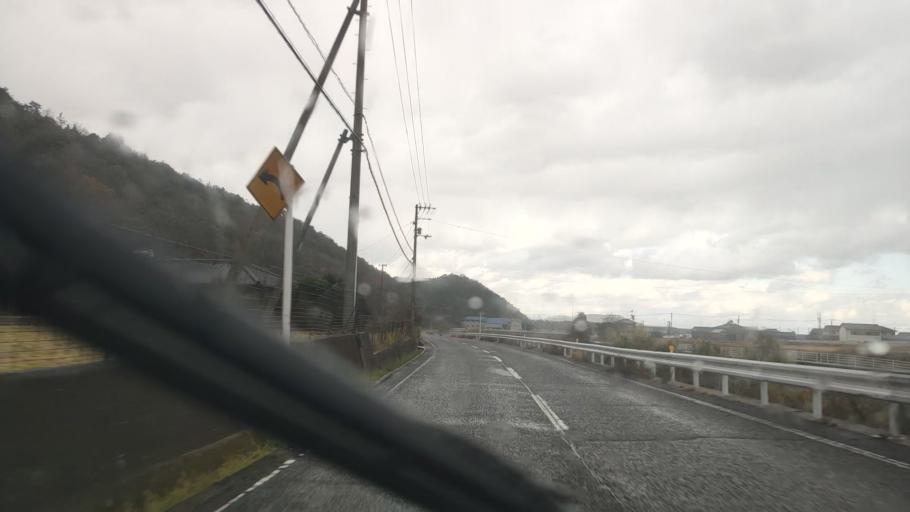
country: JP
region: Tokushima
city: Ishii
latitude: 34.2020
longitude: 134.4021
